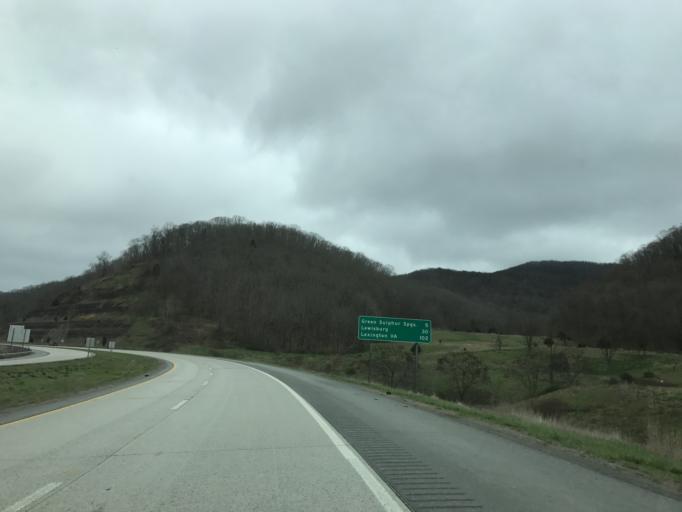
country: US
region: West Virginia
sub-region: Summers County
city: Hinton
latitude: 37.7857
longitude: -80.8803
